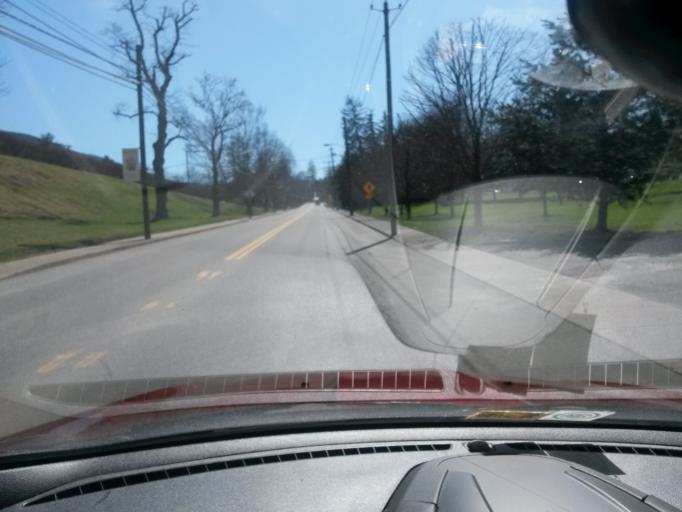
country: US
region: West Virginia
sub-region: Greenbrier County
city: White Sulphur Springs
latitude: 37.7880
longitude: -80.3044
